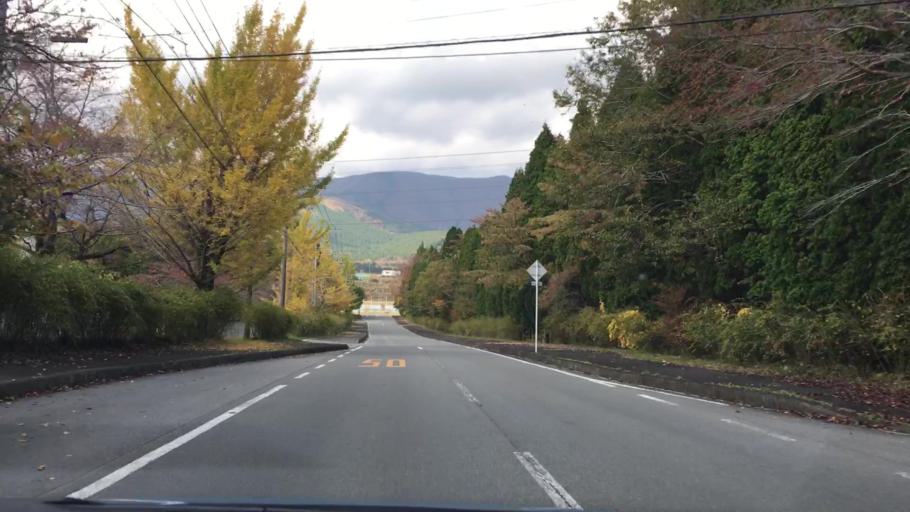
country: JP
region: Shizuoka
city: Gotemba
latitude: 35.3651
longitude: 138.9403
